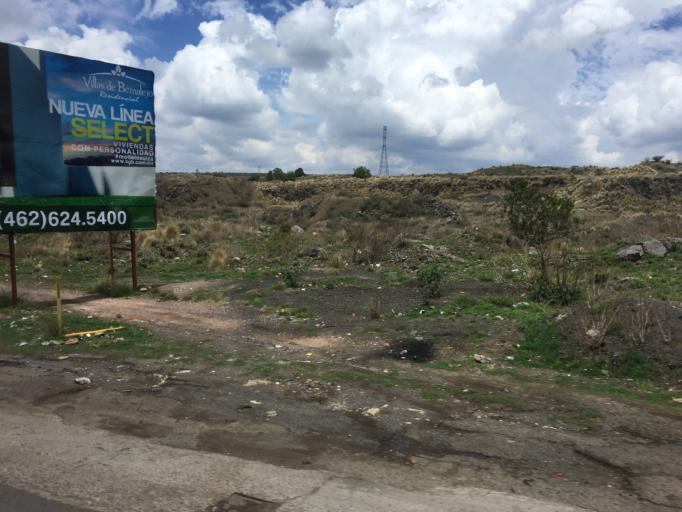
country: MX
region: Guanajuato
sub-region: Irapuato
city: Ex-Hacienda del Copal
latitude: 20.7433
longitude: -101.3404
